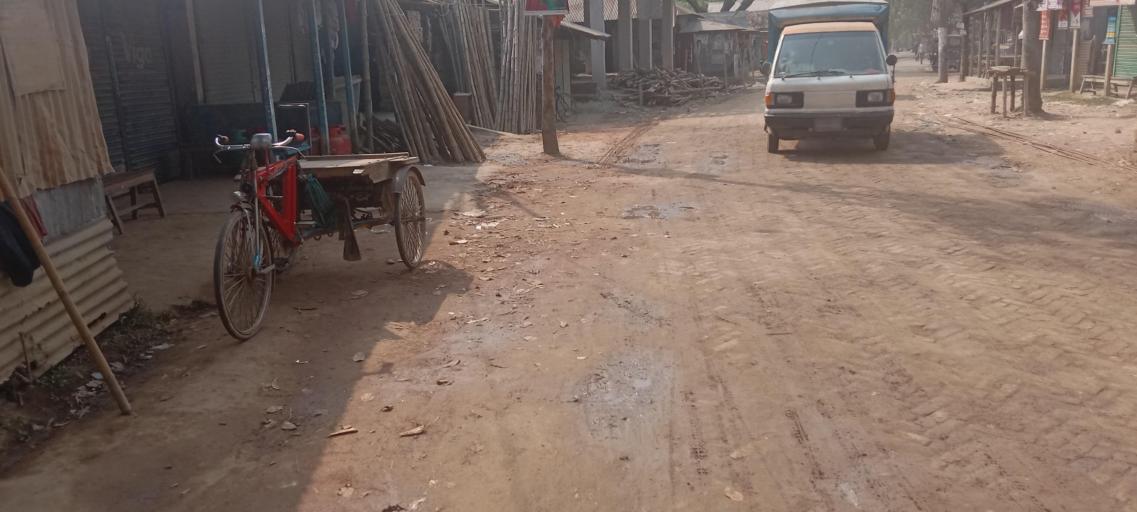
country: BD
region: Dhaka
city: Sakhipur
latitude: 24.3339
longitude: 90.2874
